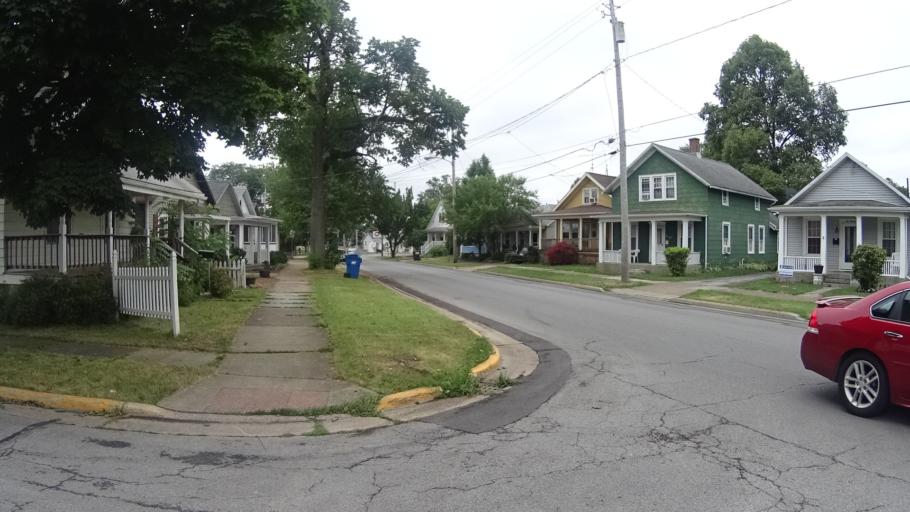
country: US
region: Ohio
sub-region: Erie County
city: Sandusky
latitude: 41.4504
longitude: -82.6977
